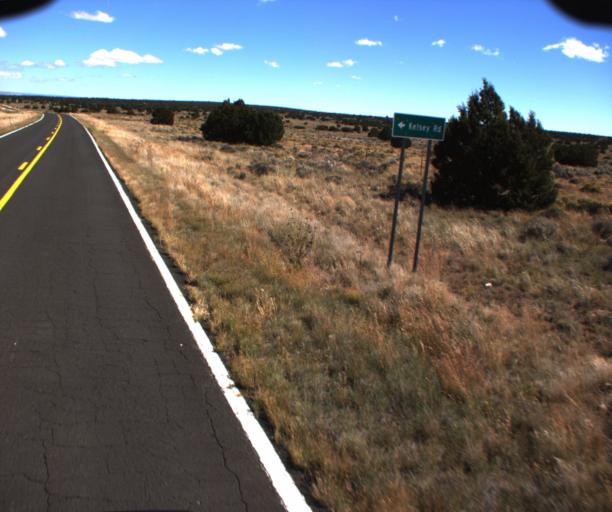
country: US
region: New Mexico
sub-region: McKinley County
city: Zuni Pueblo
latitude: 34.9913
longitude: -109.1055
